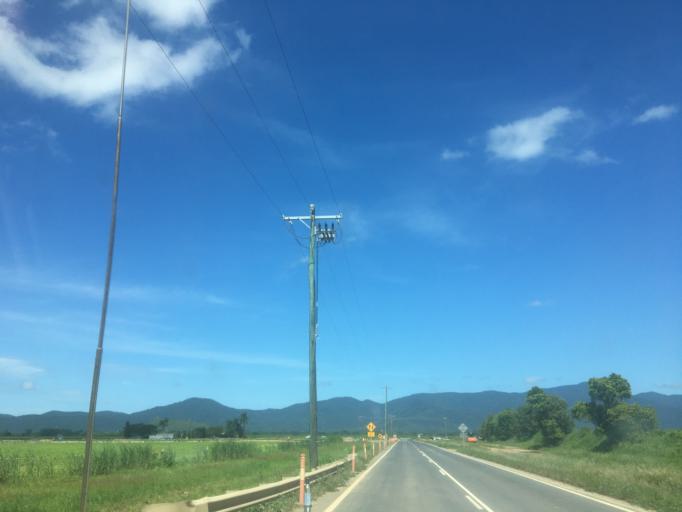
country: AU
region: Queensland
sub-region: Cairns
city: Woree
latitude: -17.0603
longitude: 145.7662
